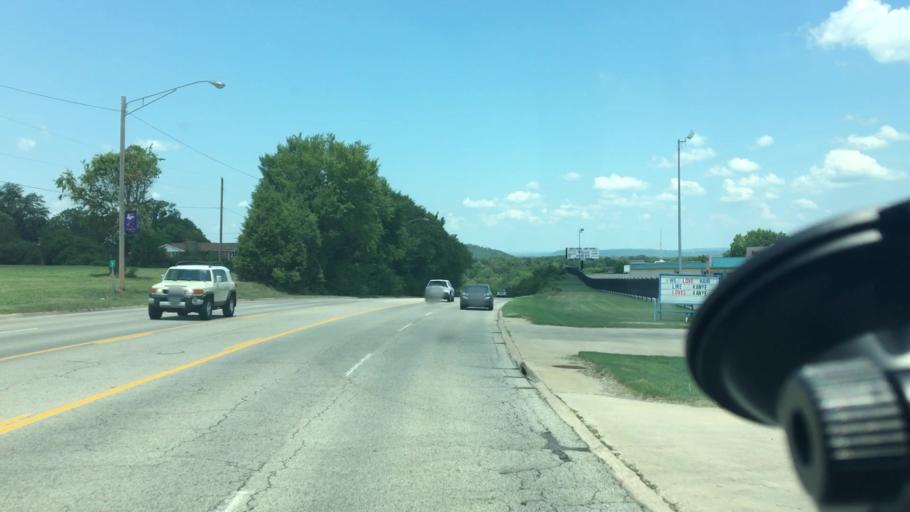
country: US
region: Arkansas
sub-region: Sebastian County
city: Barling
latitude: 35.3379
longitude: -94.3192
